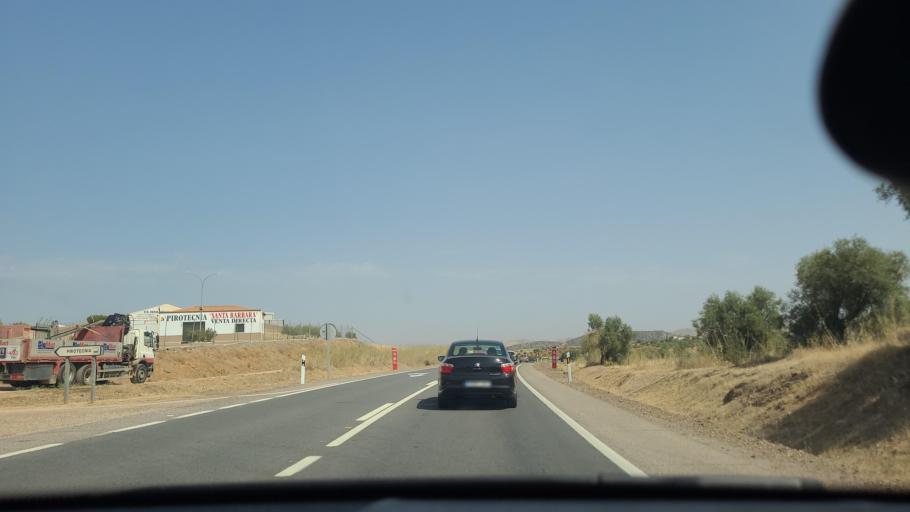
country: ES
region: Extremadura
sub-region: Provincia de Badajoz
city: Zafra
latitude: 38.4436
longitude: -6.4254
